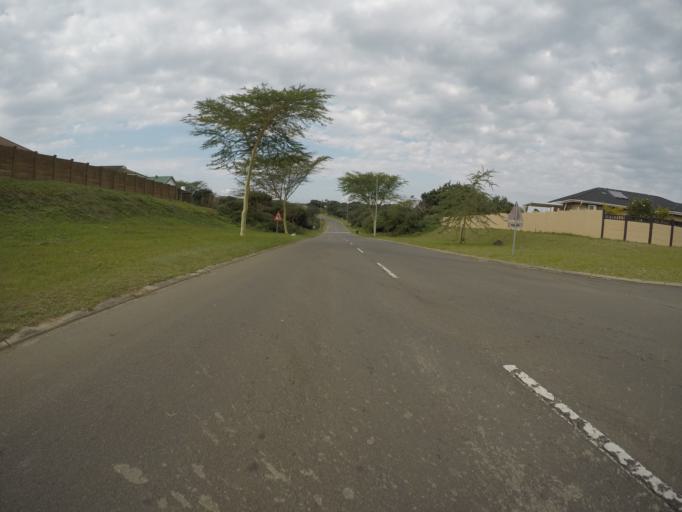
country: ZA
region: KwaZulu-Natal
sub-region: uThungulu District Municipality
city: Richards Bay
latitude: -28.7370
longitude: 32.0904
